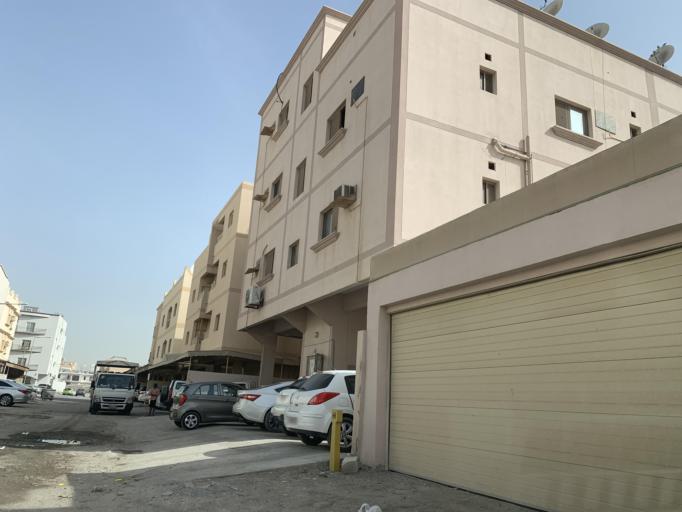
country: BH
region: Northern
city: Madinat `Isa
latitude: 26.1781
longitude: 50.5665
